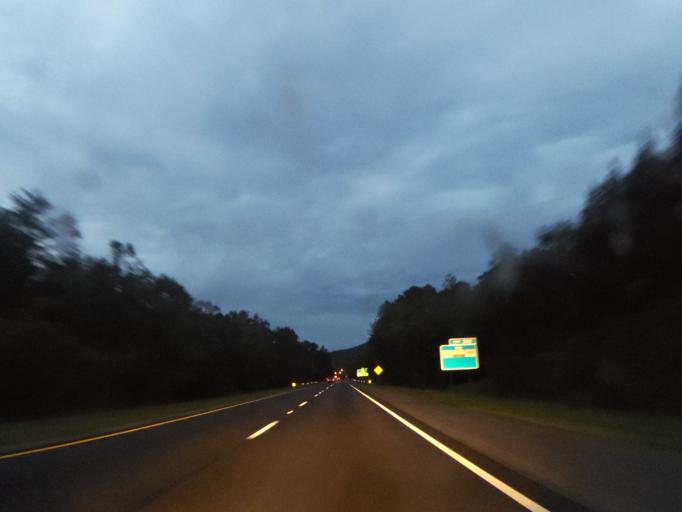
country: US
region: Alabama
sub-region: DeKalb County
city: Collinsville
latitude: 34.2690
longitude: -85.8846
